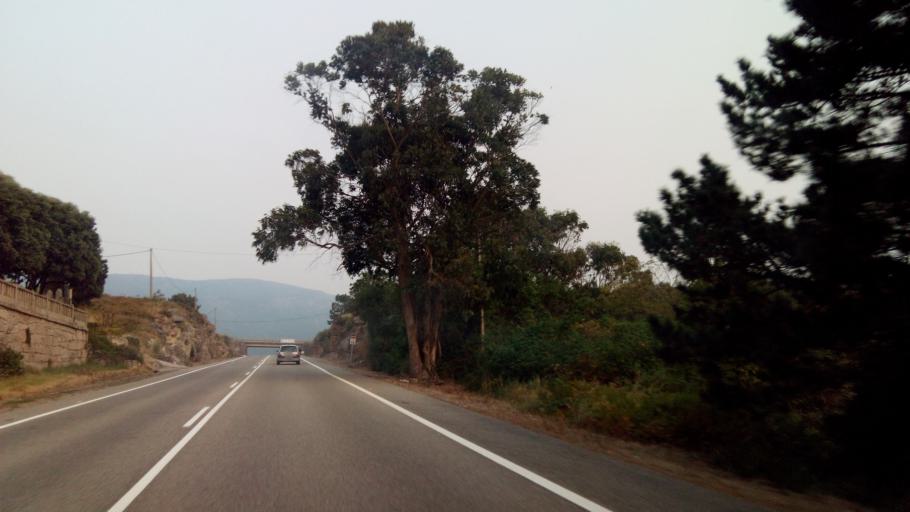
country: ES
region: Galicia
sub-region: Provincia de Pontevedra
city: Oia
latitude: 42.0557
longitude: -8.8868
